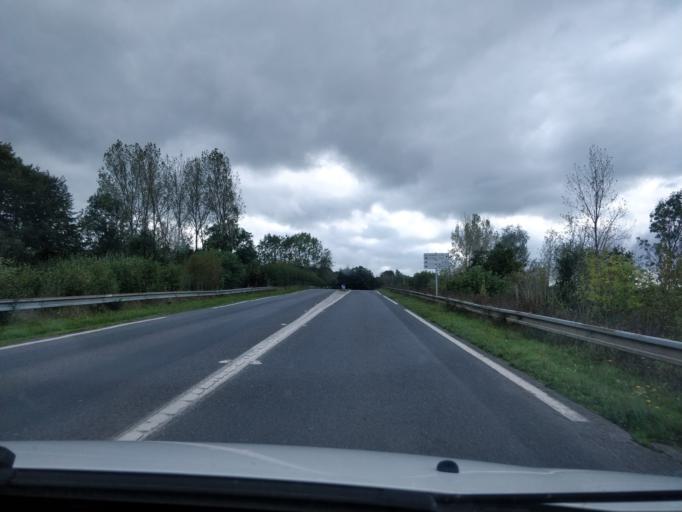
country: FR
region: Lower Normandy
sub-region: Departement de la Manche
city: Villedieu-les-Poeles
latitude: 48.8346
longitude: -1.2042
